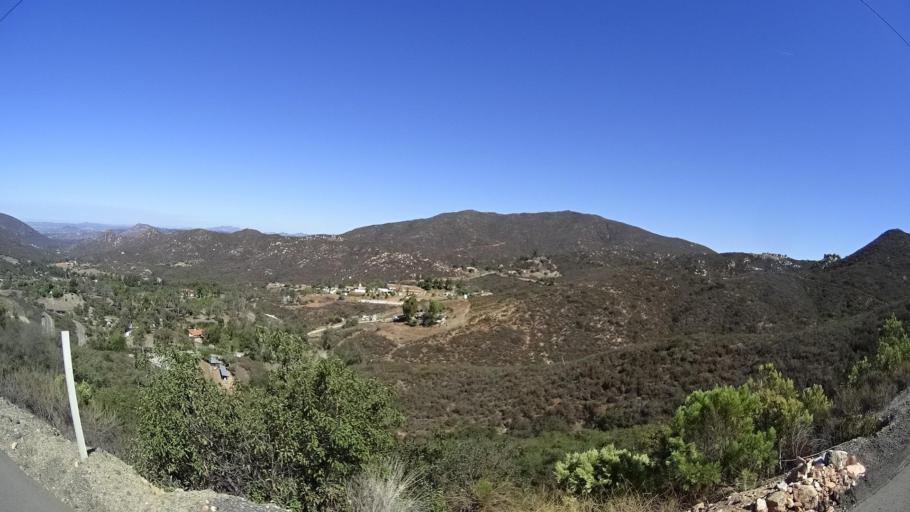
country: US
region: California
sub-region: San Diego County
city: Jamul
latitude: 32.7334
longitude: -116.8141
